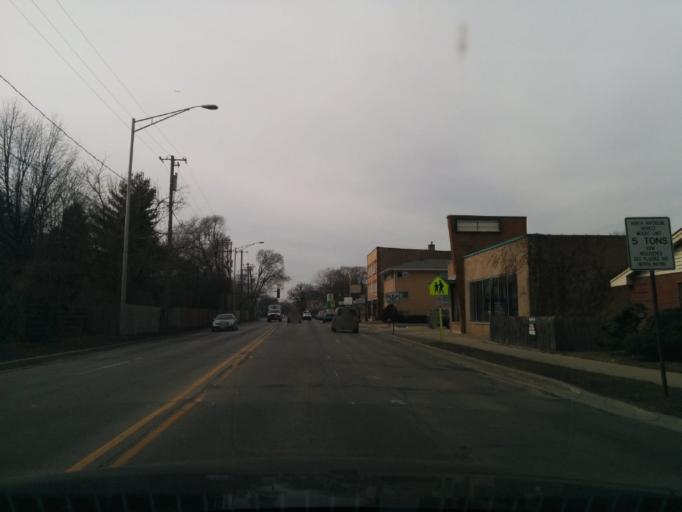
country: US
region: Illinois
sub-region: Cook County
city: North Riverside
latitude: 41.8429
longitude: -87.8208
